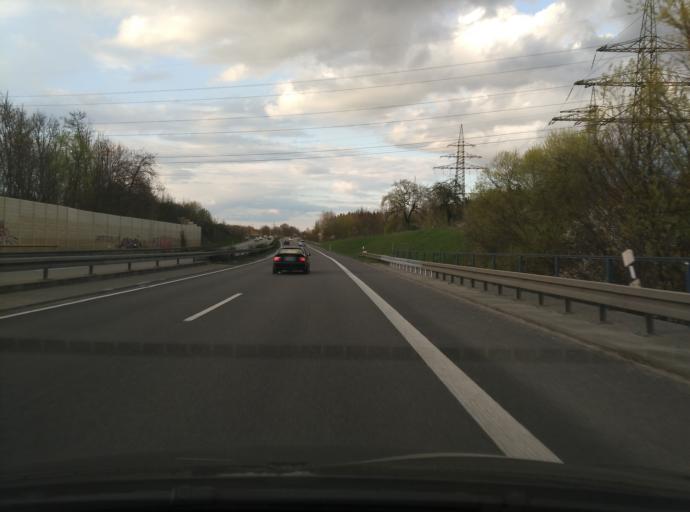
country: DE
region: Baden-Wuerttemberg
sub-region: Tuebingen Region
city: Eningen unter Achalm
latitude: 48.5135
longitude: 9.2439
